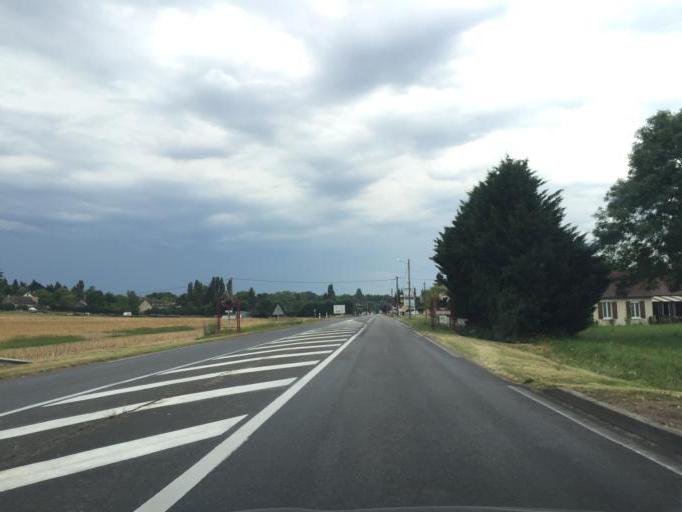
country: FR
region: Auvergne
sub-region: Departement de l'Allier
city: Varennes-sur-Allier
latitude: 46.3555
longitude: 3.3752
